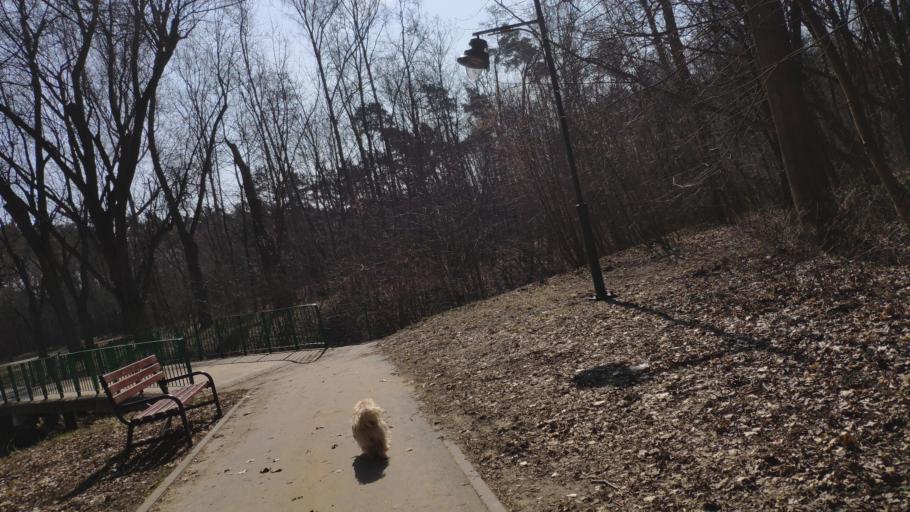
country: PL
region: Lodz Voivodeship
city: Lodz
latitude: 51.7691
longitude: 19.4050
